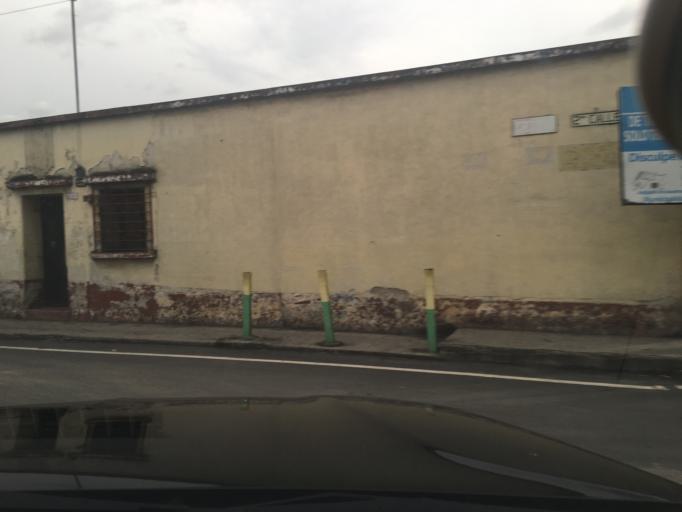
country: GT
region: Guatemala
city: Amatitlan
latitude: 14.4823
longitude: -90.6170
